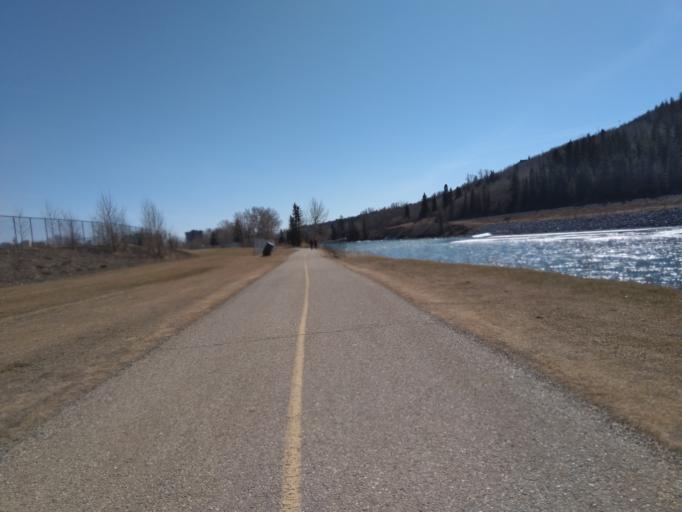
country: CA
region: Alberta
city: Calgary
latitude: 51.0704
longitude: -114.1708
